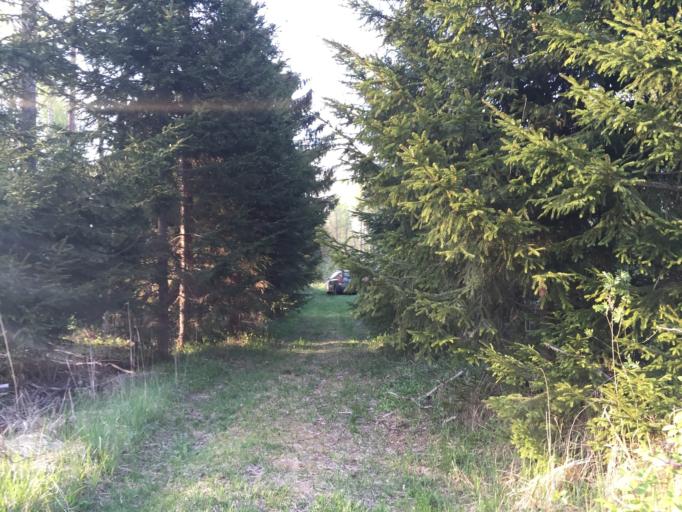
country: LV
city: Tireli
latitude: 56.8437
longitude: 23.7087
